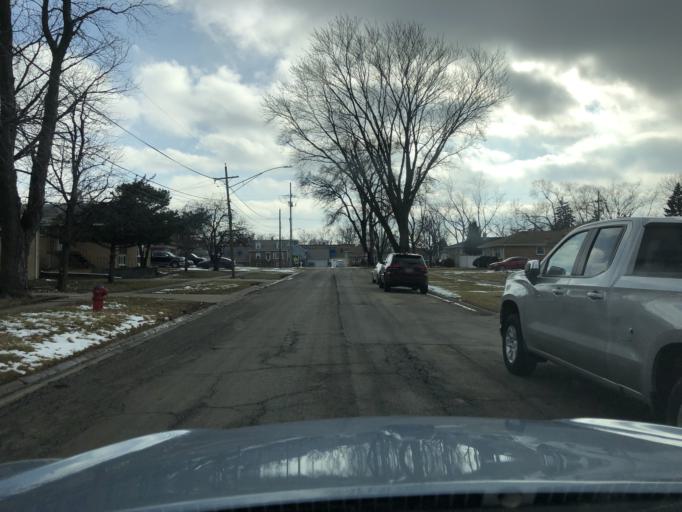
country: US
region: Illinois
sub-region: Cook County
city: Schiller Park
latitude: 41.9522
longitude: -87.8771
